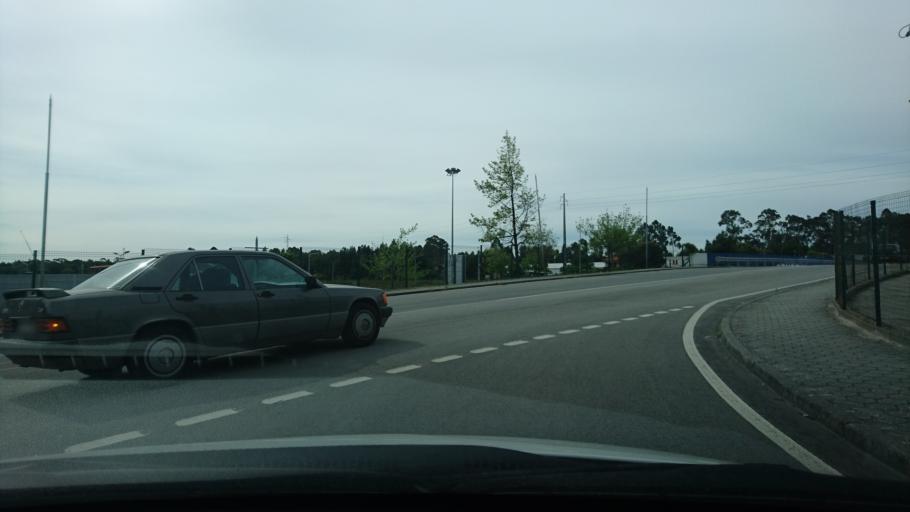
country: PT
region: Aveiro
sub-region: Aveiro
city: Aveiro
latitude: 40.6451
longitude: -8.6087
